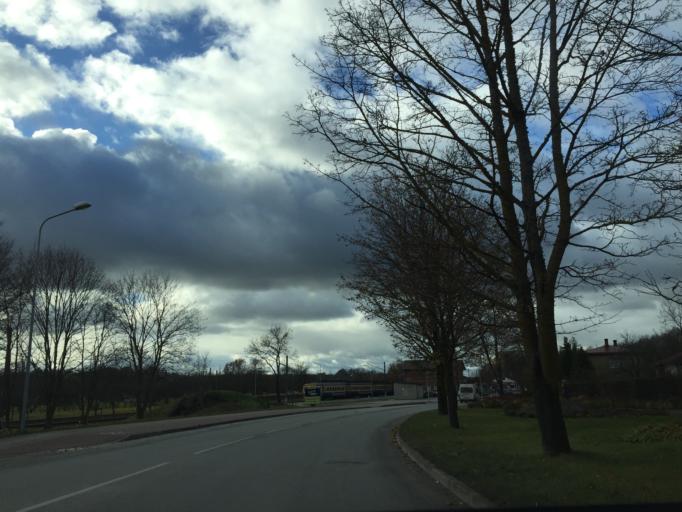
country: LV
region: Tukuma Rajons
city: Tukums
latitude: 56.9669
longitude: 23.1727
